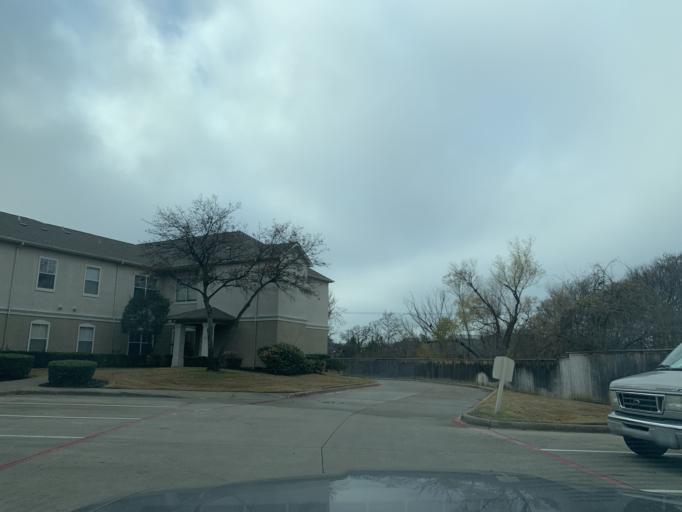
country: US
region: Texas
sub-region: Tarrant County
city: Bedford
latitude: 32.8405
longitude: -97.1438
